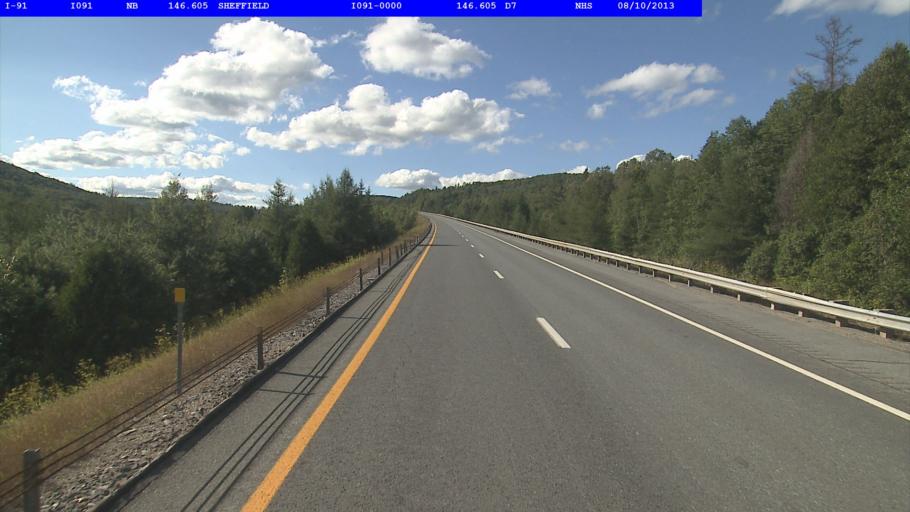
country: US
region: Vermont
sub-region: Caledonia County
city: Lyndonville
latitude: 44.6173
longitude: -72.1203
